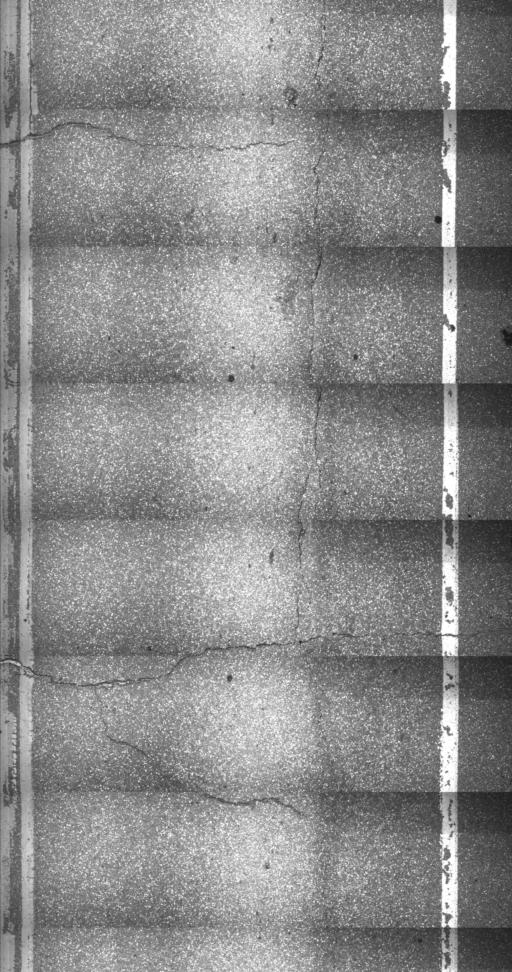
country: US
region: Vermont
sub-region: Orleans County
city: Newport
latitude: 44.9271
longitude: -72.2883
